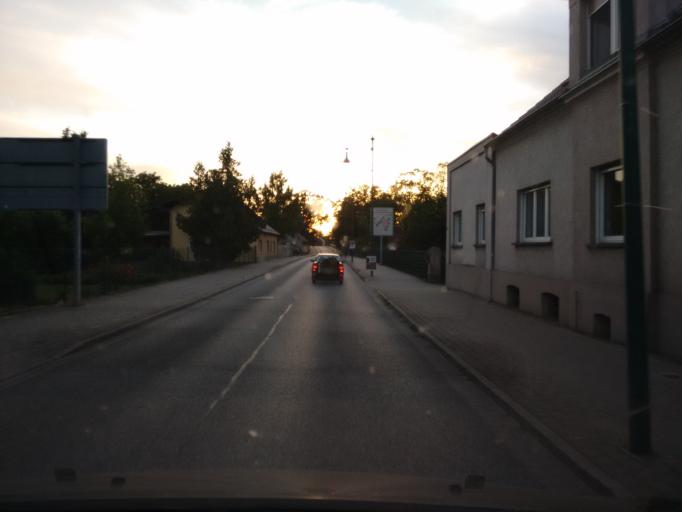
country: DE
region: Brandenburg
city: Beeskow
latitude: 52.1678
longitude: 14.2578
